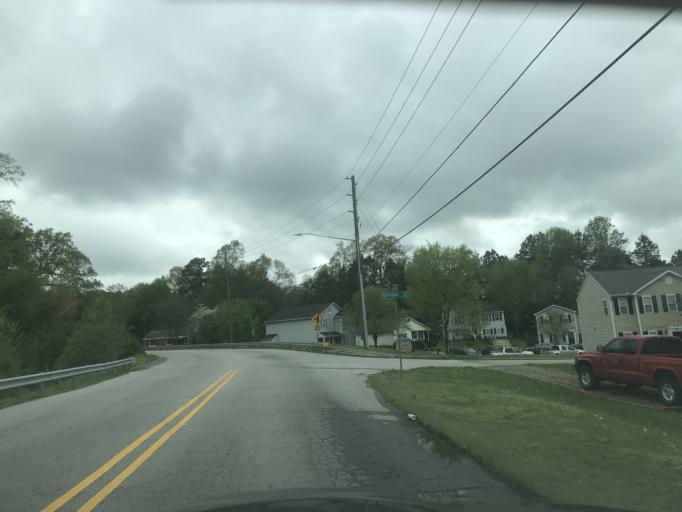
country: US
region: North Carolina
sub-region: Wake County
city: Raleigh
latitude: 35.7506
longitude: -78.6592
